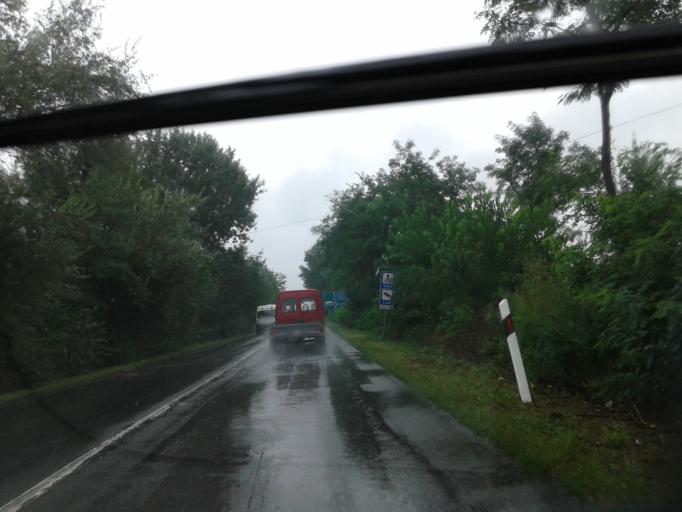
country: HU
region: Csongrad
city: Asotthalom
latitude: 46.2265
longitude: 19.8289
